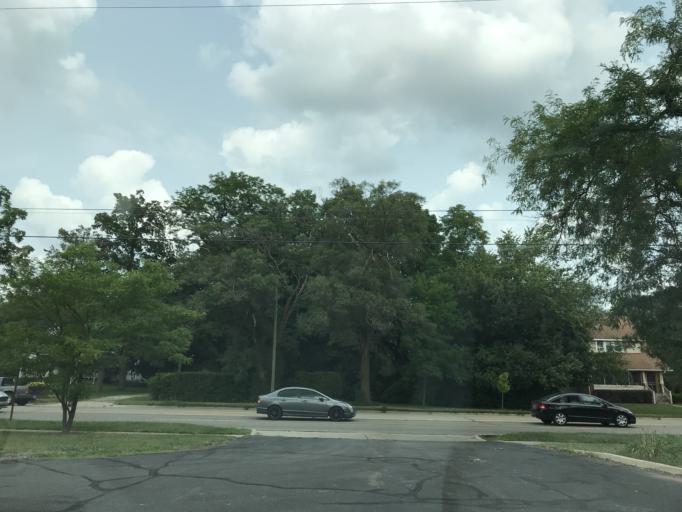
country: US
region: Michigan
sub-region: Washtenaw County
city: Ann Arbor
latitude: 42.2449
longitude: -83.6956
